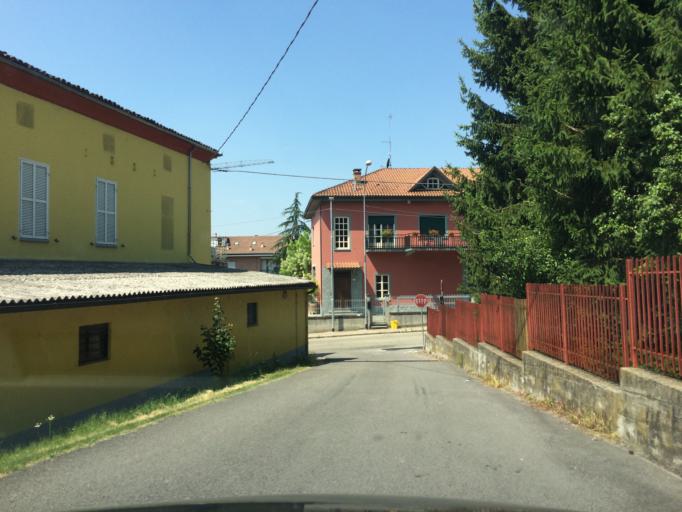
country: IT
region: Piedmont
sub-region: Provincia di Asti
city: Costigliole d'Asti
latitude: 44.7609
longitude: 8.2030
